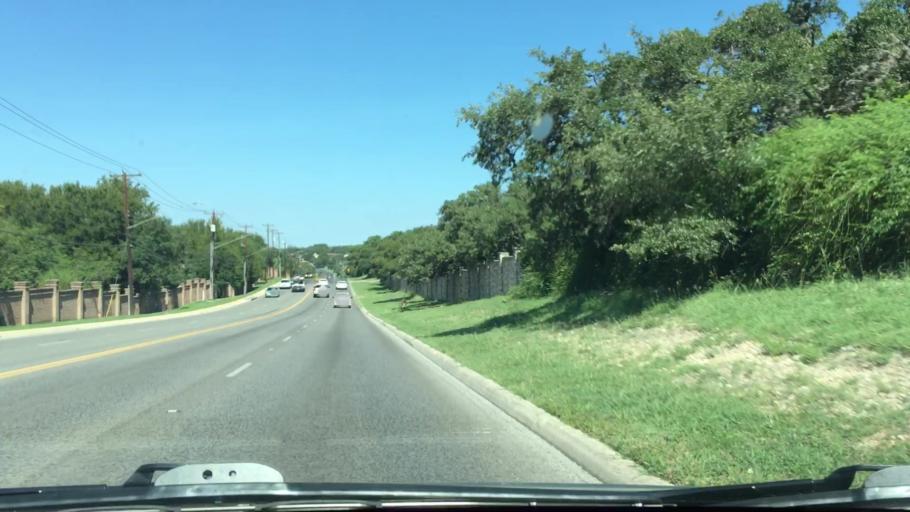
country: US
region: Texas
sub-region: Bexar County
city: Hollywood Park
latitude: 29.5762
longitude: -98.4969
